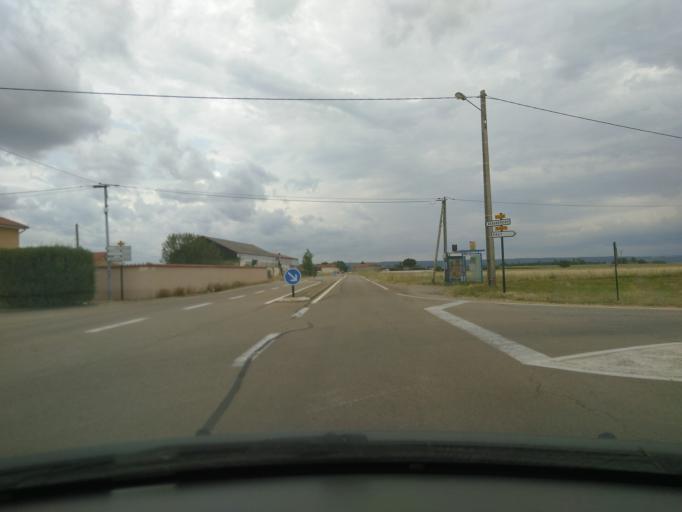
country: FR
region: Rhone-Alpes
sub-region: Departement de l'Isere
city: Beaurepaire
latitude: 45.3695
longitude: 5.0275
